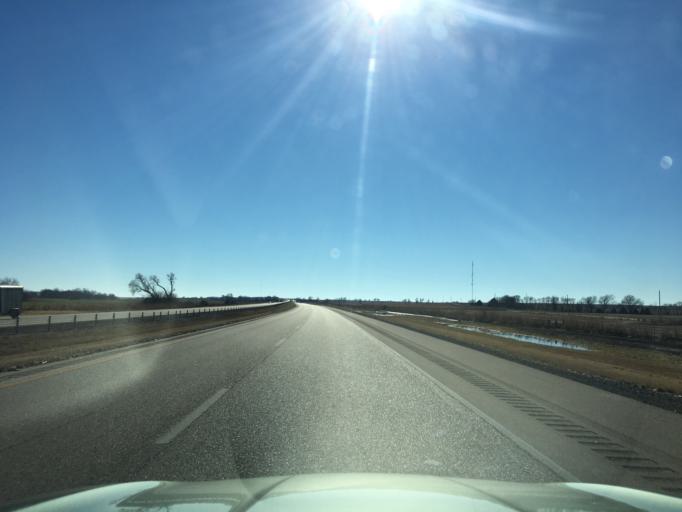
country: US
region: Oklahoma
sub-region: Kay County
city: Blackwell
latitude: 36.8947
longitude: -97.3541
